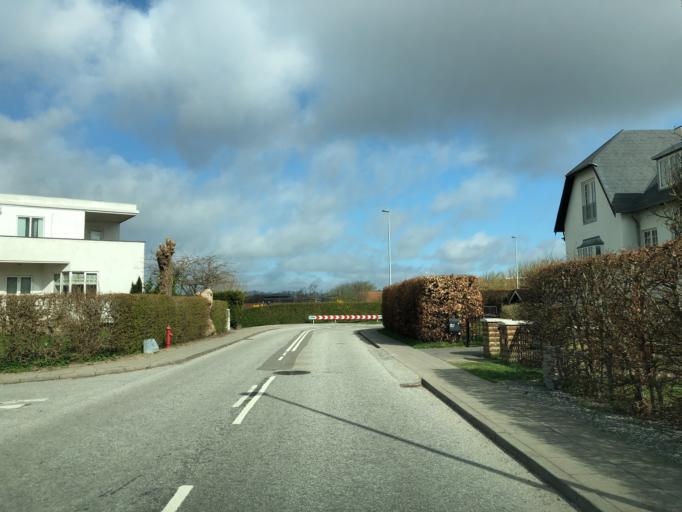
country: DK
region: North Denmark
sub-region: Alborg Kommune
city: Aalborg
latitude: 57.0490
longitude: 9.8943
